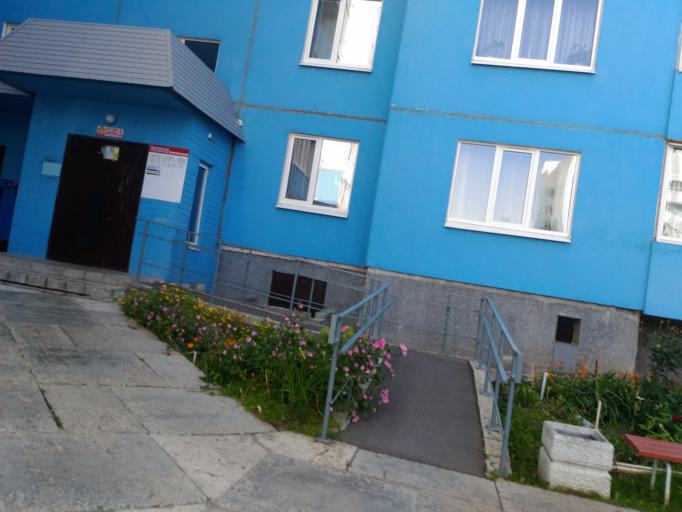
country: RU
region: Ulyanovsk
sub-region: Ulyanovskiy Rayon
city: Ulyanovsk
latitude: 54.3473
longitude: 48.3397
